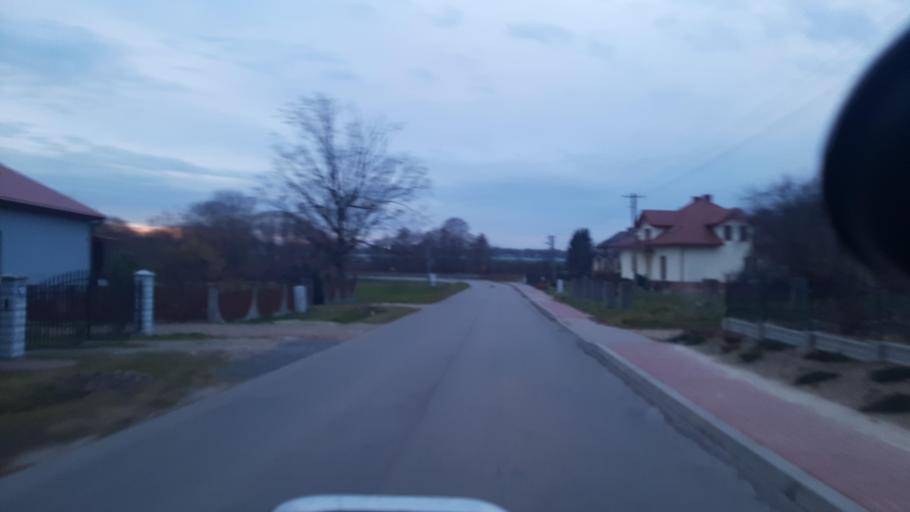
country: PL
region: Lublin Voivodeship
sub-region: Powiat lubelski
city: Garbow
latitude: 51.3575
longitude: 22.3721
